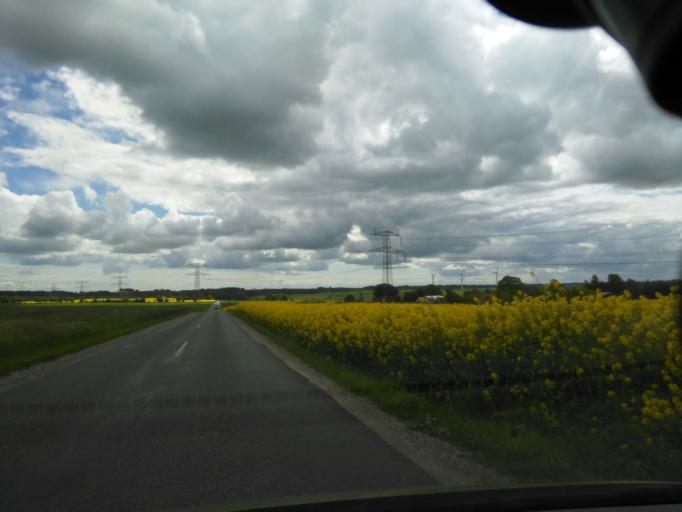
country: DK
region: Central Jutland
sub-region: Arhus Kommune
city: Kolt
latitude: 56.0842
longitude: 10.0814
